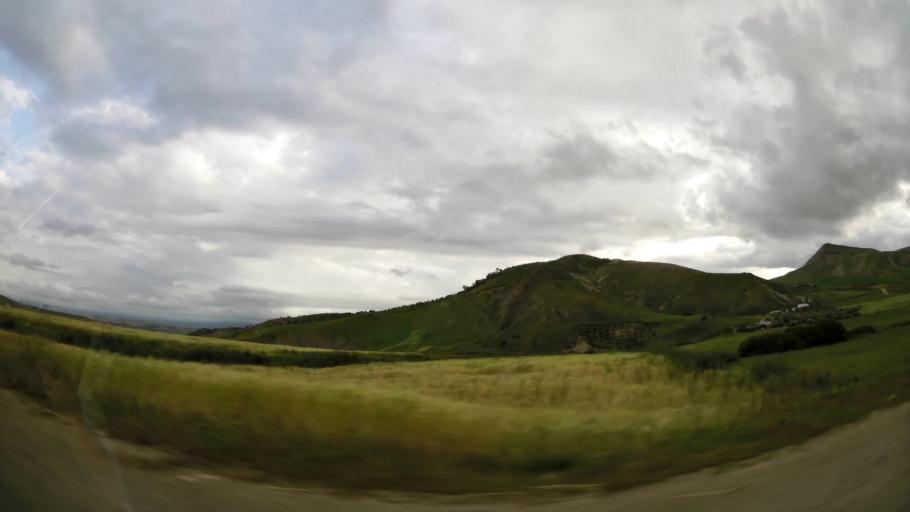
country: MA
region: Taza-Al Hoceima-Taounate
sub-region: Taza
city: Taza
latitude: 34.2893
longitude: -3.9647
